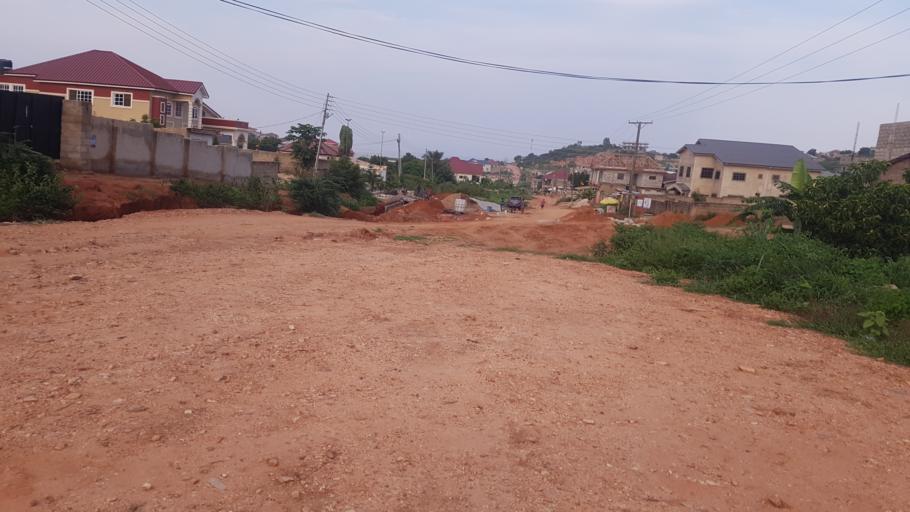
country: GH
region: Greater Accra
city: Gbawe
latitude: 5.5234
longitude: -0.3445
